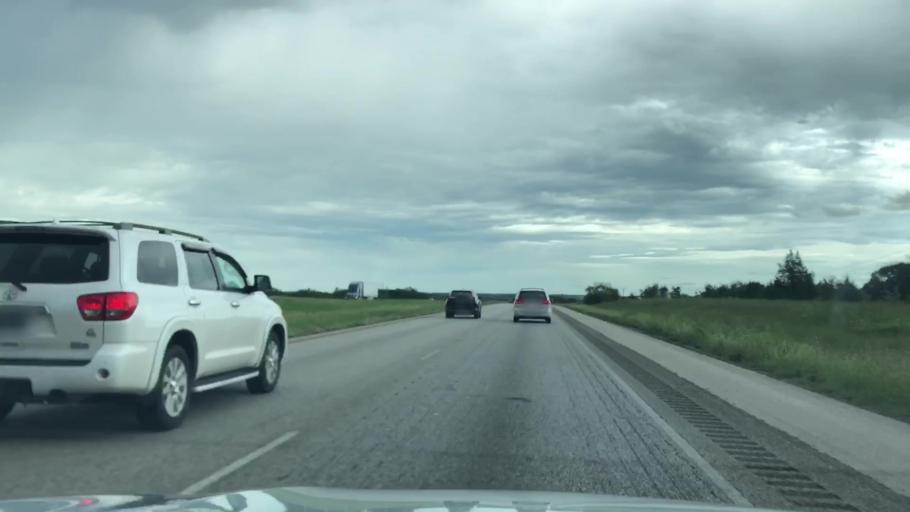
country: US
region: Texas
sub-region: Fayette County
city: Schulenburg
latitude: 29.6892
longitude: -96.9627
